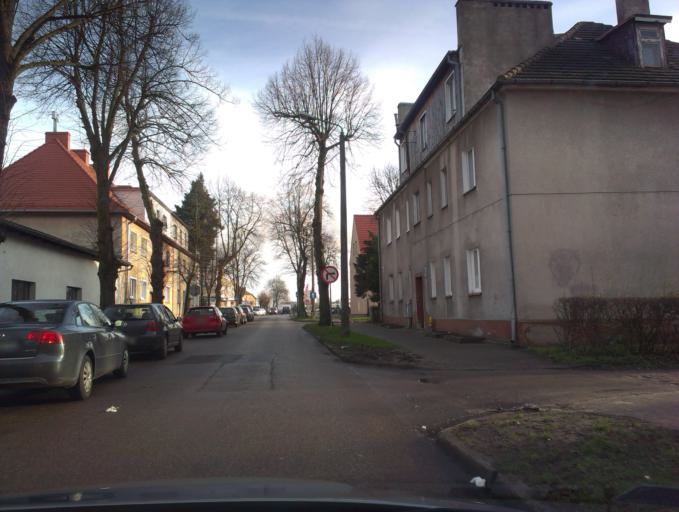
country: PL
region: West Pomeranian Voivodeship
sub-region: Powiat szczecinecki
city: Szczecinek
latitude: 53.6974
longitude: 16.7032
